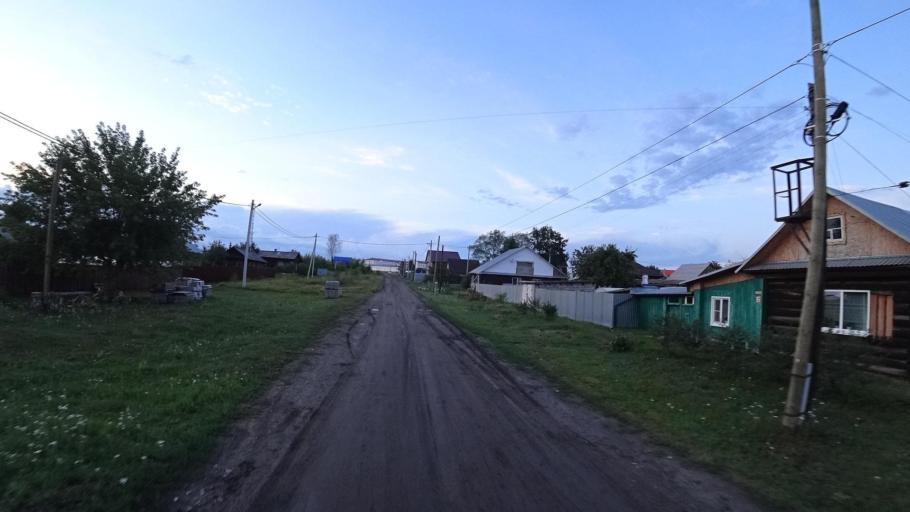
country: RU
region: Sverdlovsk
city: Kamyshlov
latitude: 56.8532
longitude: 62.7324
